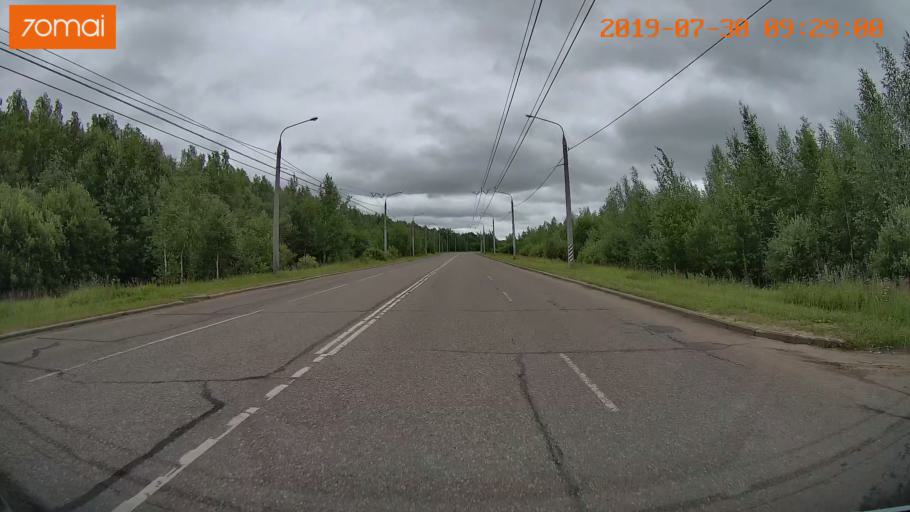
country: RU
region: Ivanovo
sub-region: Gorod Ivanovo
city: Ivanovo
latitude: 56.9482
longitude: 40.9471
